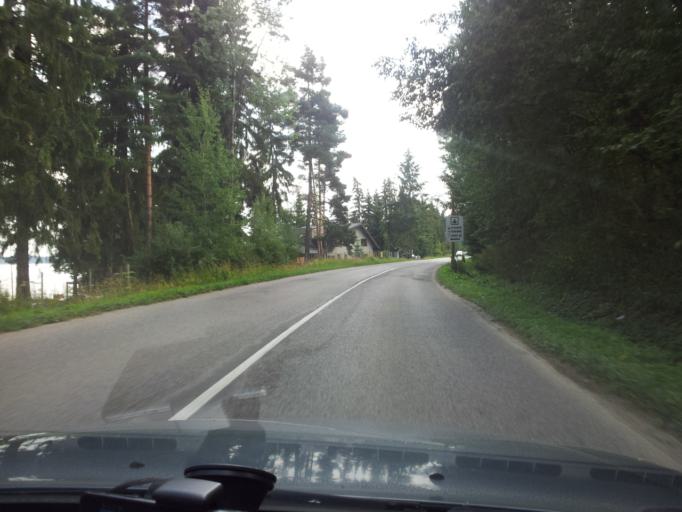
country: SK
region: Zilinsky
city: Namestovo
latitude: 49.4019
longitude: 19.5109
